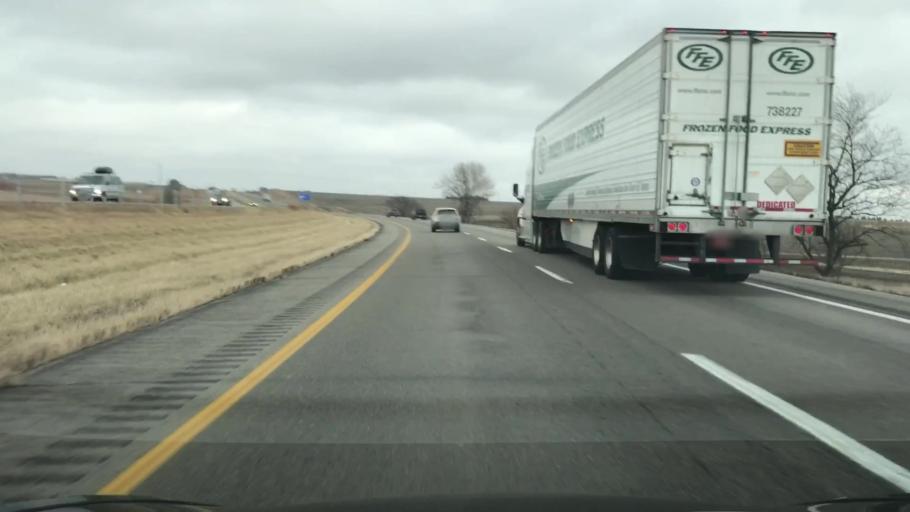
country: US
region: Iowa
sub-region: Guthrie County
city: Stuart
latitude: 41.4932
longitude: -94.3607
